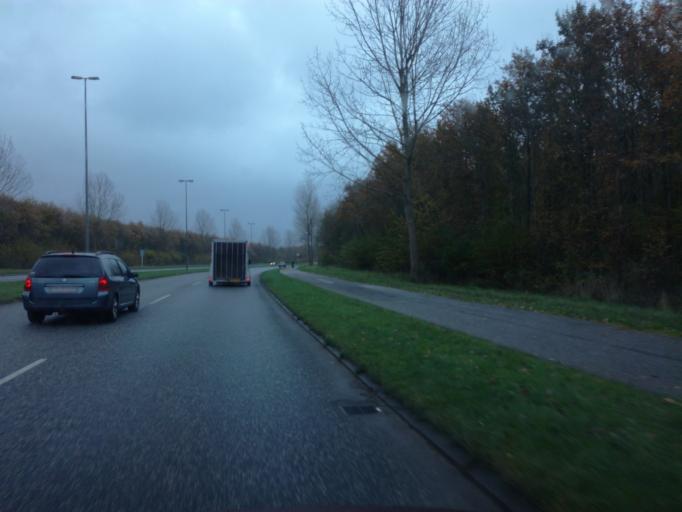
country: DK
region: South Denmark
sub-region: Fredericia Kommune
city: Fredericia
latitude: 55.5868
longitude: 9.7402
